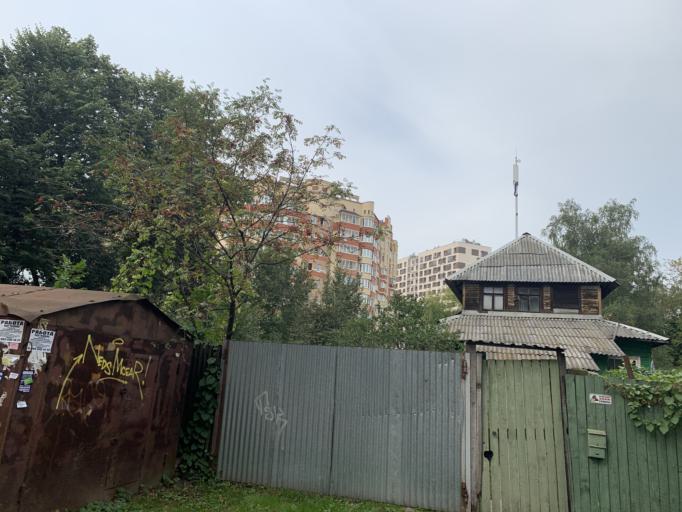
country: RU
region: Moscow
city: Yaroslavskiy
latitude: 55.8889
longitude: 37.7235
